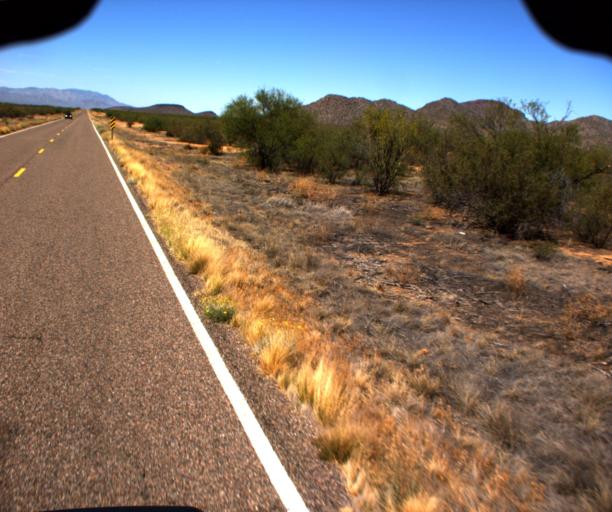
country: US
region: Arizona
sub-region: Yavapai County
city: Congress
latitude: 34.0415
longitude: -113.0697
